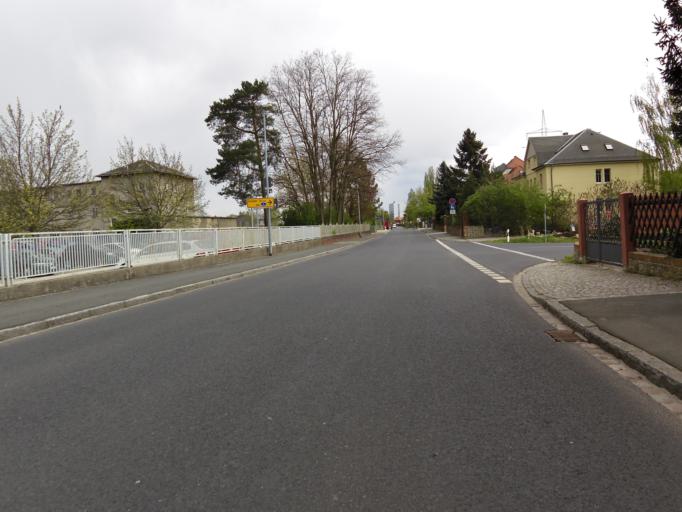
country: DE
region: Saxony
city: Coswig
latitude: 51.1135
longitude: 13.5848
